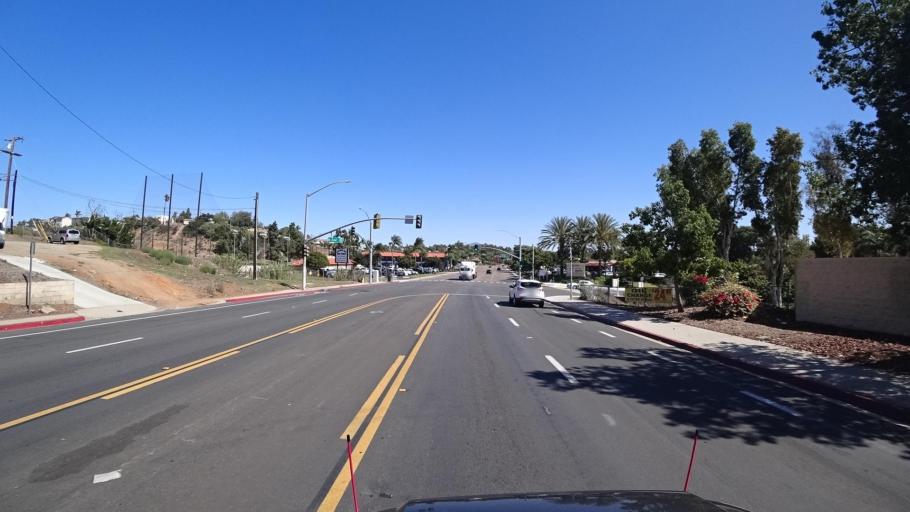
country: US
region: California
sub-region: San Diego County
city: Chula Vista
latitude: 32.6609
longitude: -117.0850
